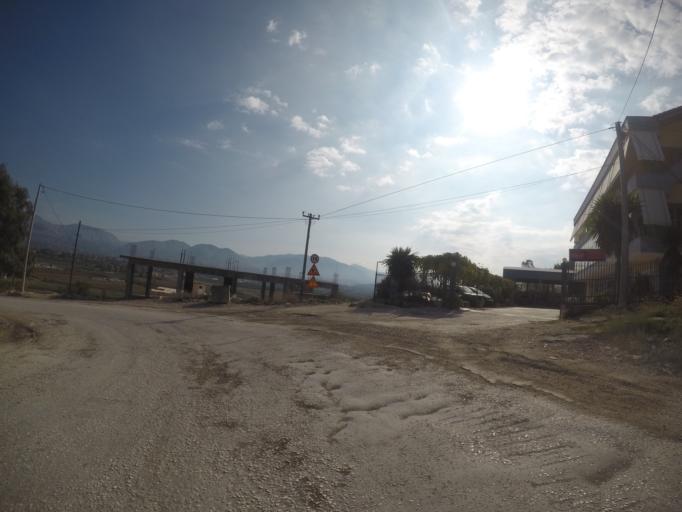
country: AL
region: Vlore
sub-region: Rrethi i Sarandes
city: Sarande
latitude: 39.8754
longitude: 20.0318
